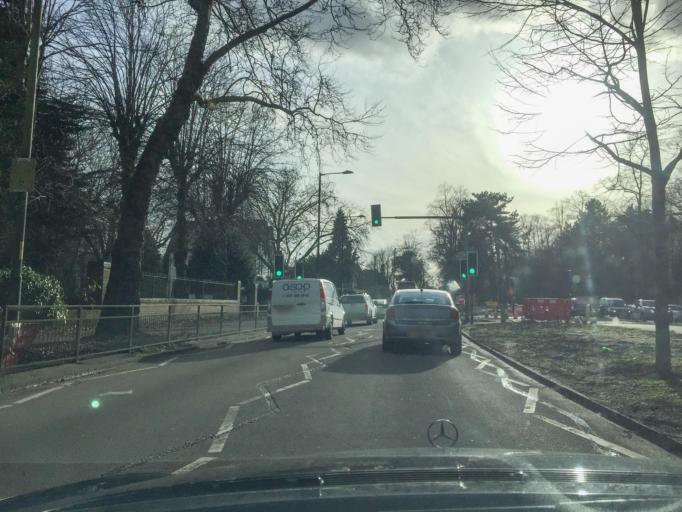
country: GB
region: England
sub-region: City and Borough of Birmingham
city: Birmingham
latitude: 52.4530
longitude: -1.9130
